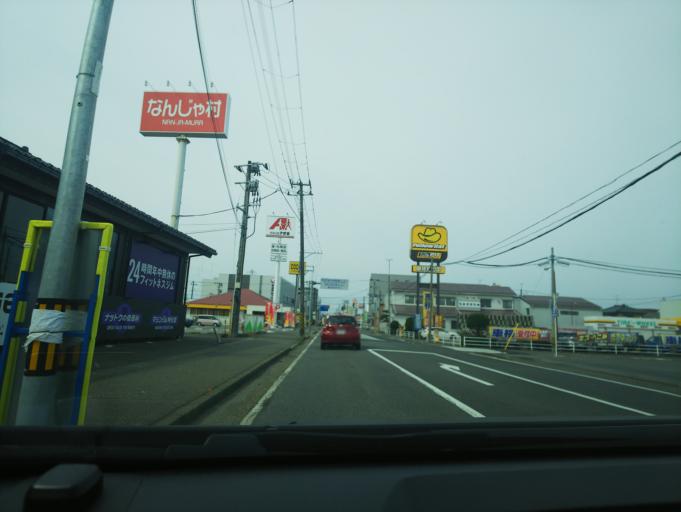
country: JP
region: Niigata
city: Niigata-shi
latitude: 37.9021
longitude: 139.0703
